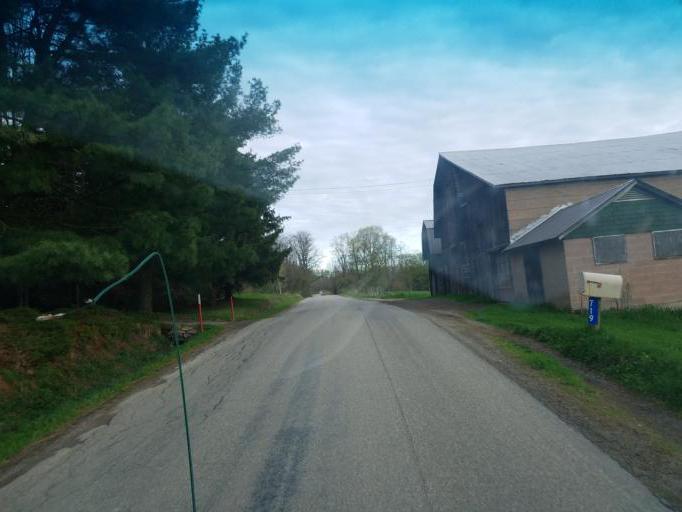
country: US
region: Pennsylvania
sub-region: Tioga County
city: Westfield
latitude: 41.9599
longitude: -77.7059
